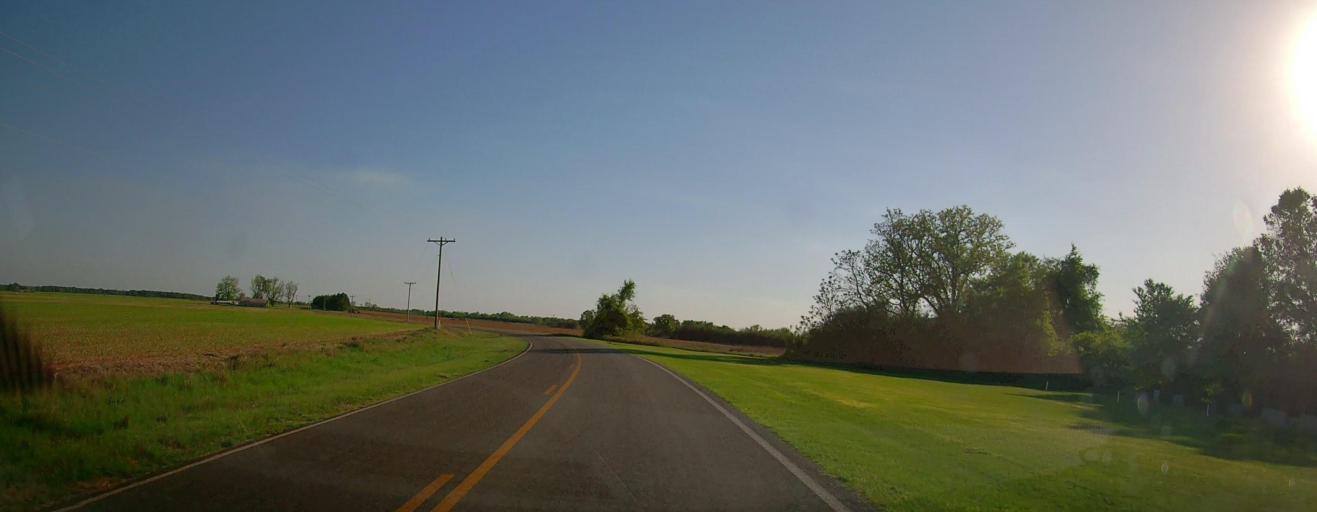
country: US
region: Georgia
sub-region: Macon County
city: Montezuma
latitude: 32.3534
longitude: -83.9430
